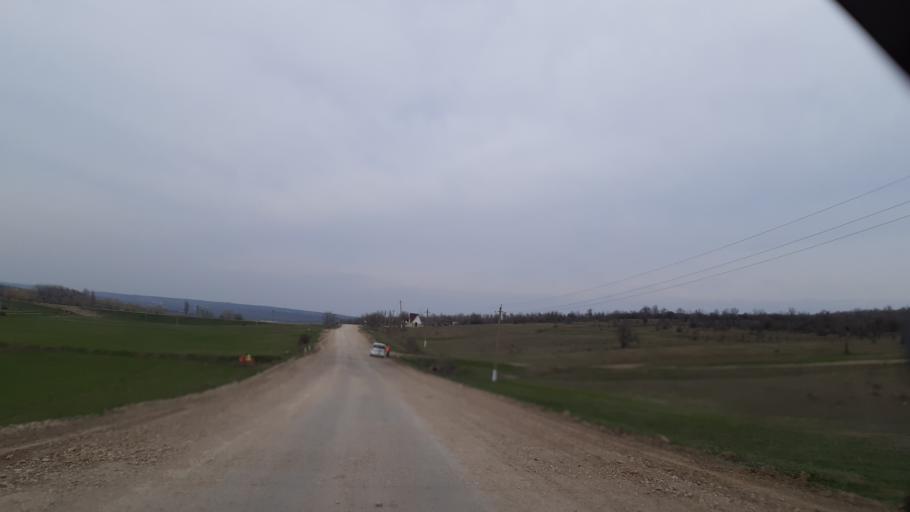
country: MD
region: Soldanesti
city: Soldanesti
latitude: 47.6292
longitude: 28.6592
